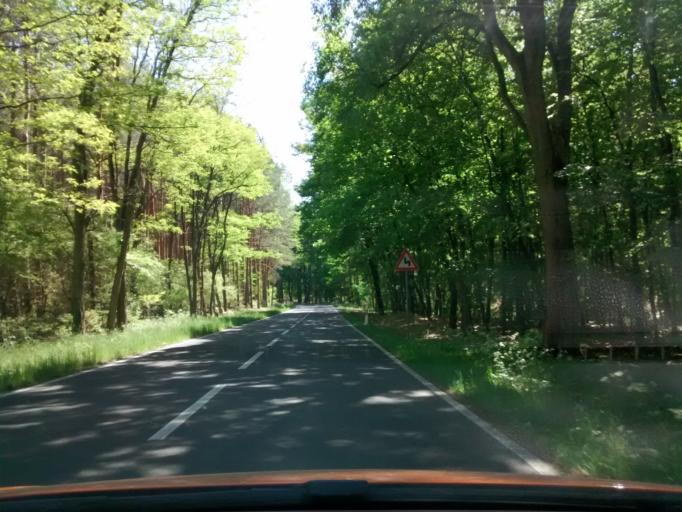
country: DE
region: Brandenburg
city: Reichenwalde
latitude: 52.2316
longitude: 13.9956
